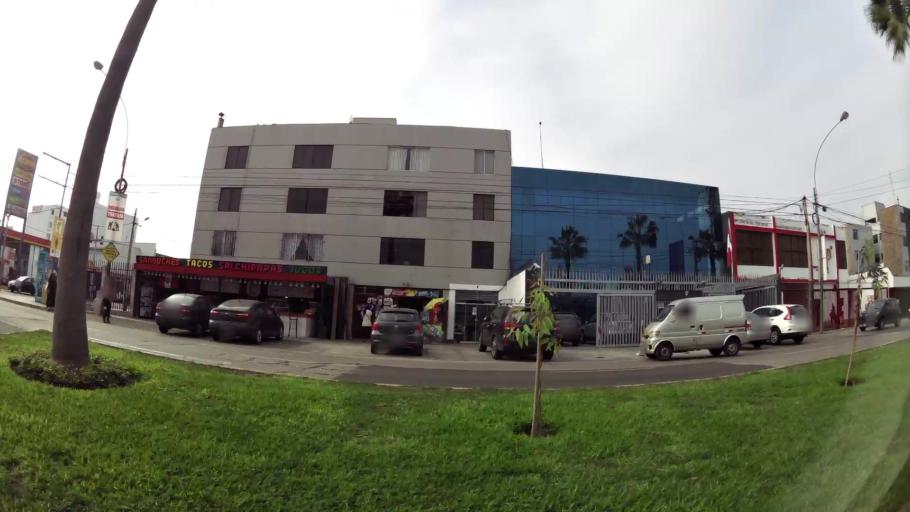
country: PE
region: Lima
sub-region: Lima
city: San Isidro
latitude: -12.1008
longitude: -77.0615
